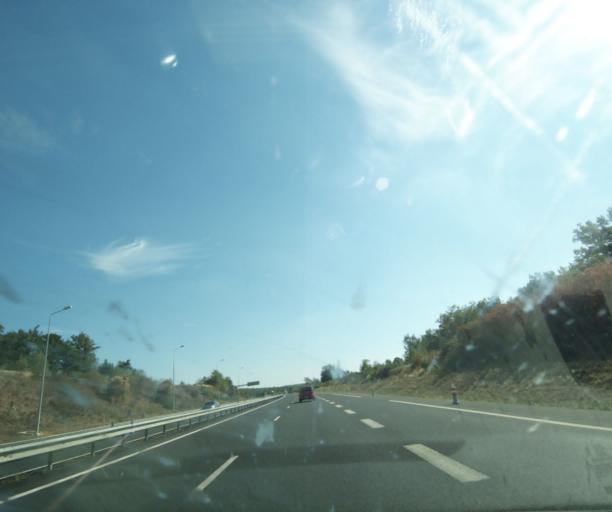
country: FR
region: Limousin
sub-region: Departement de la Correze
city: Cosnac
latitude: 45.0283
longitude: 1.5290
